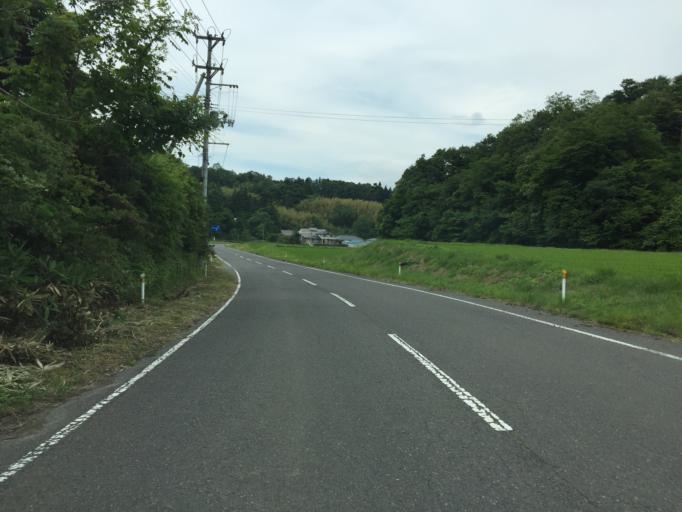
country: JP
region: Fukushima
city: Funehikimachi-funehiki
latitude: 37.4144
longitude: 140.6495
